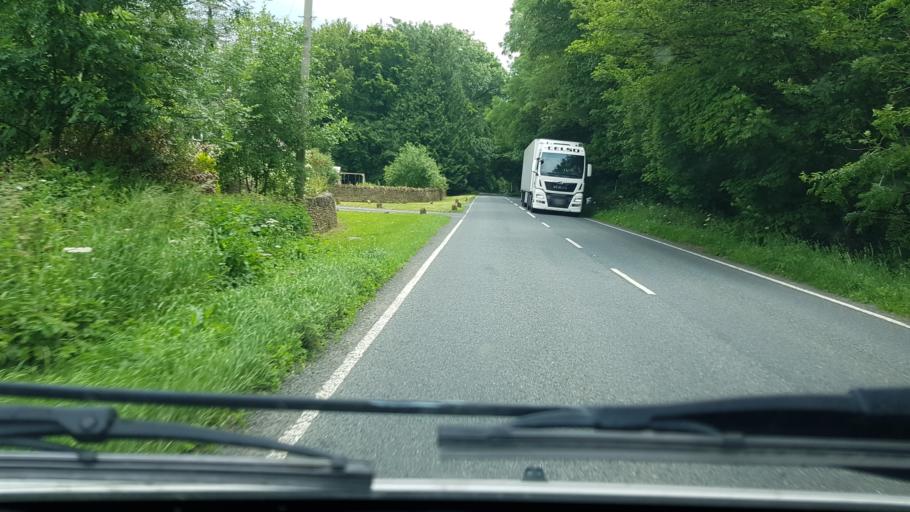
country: GB
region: England
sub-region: Gloucestershire
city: Donnington
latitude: 51.9841
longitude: -1.7687
